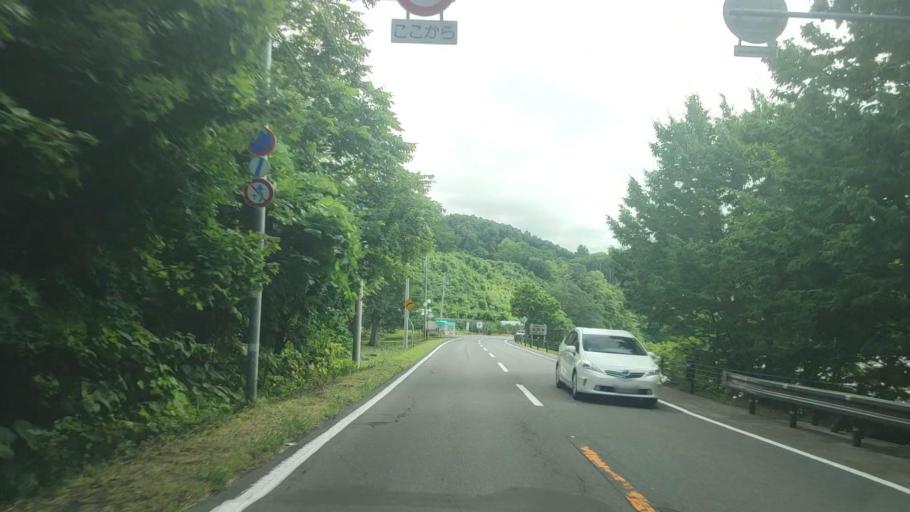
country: JP
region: Hokkaido
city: Date
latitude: 42.5615
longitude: 140.8779
